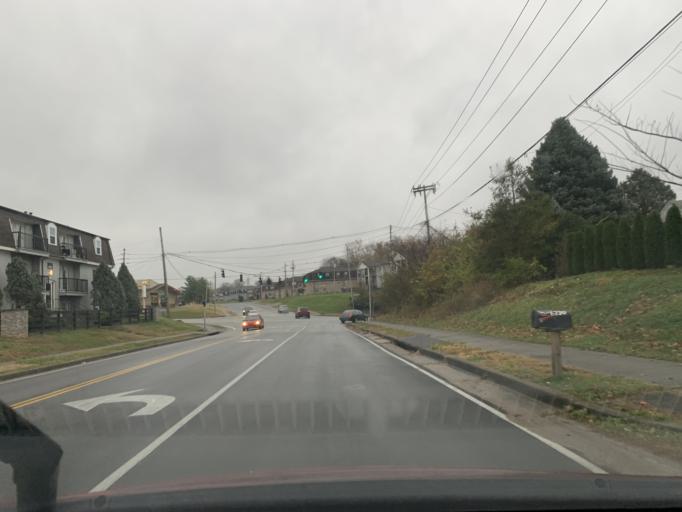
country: US
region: Kentucky
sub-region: Jefferson County
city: Buechel
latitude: 38.1976
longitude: -85.6261
